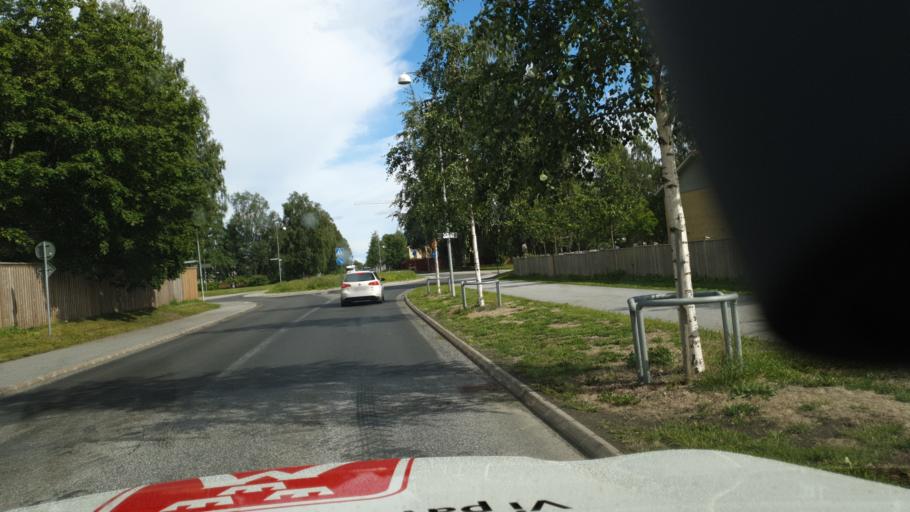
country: SE
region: Vaesterbotten
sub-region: Umea Kommun
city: Roback
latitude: 63.8355
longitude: 20.1954
